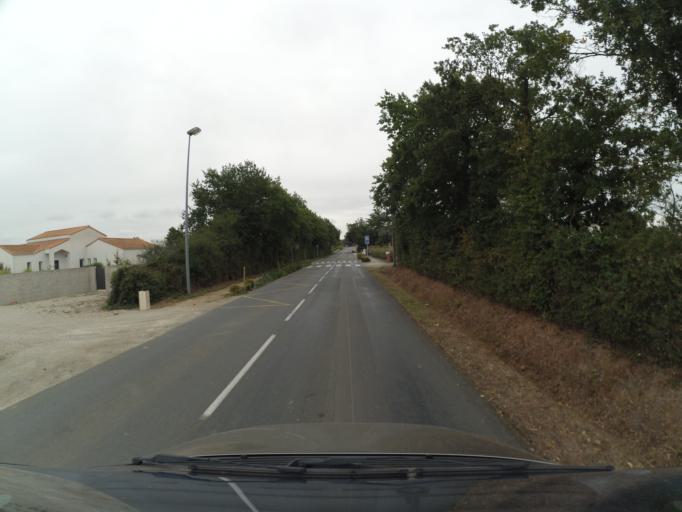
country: FR
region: Pays de la Loire
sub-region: Departement de la Vendee
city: Saint-Andre-Treize-Voies
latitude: 46.9152
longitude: -1.3845
